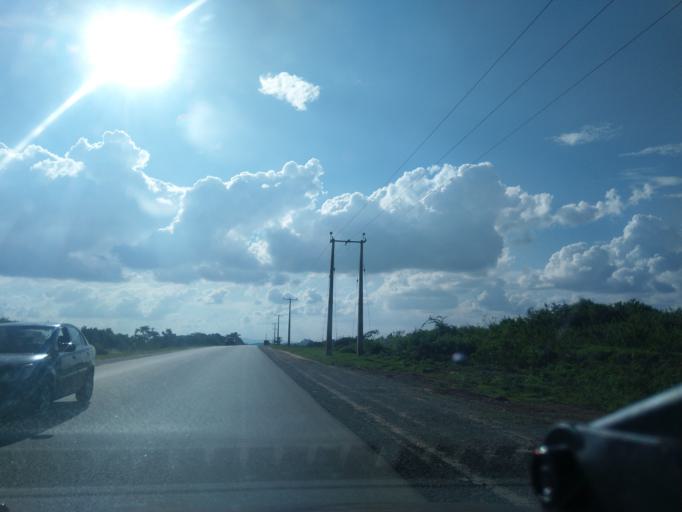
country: NG
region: Abuja Federal Capital Territory
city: Abuja
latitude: 9.0384
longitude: 7.4032
